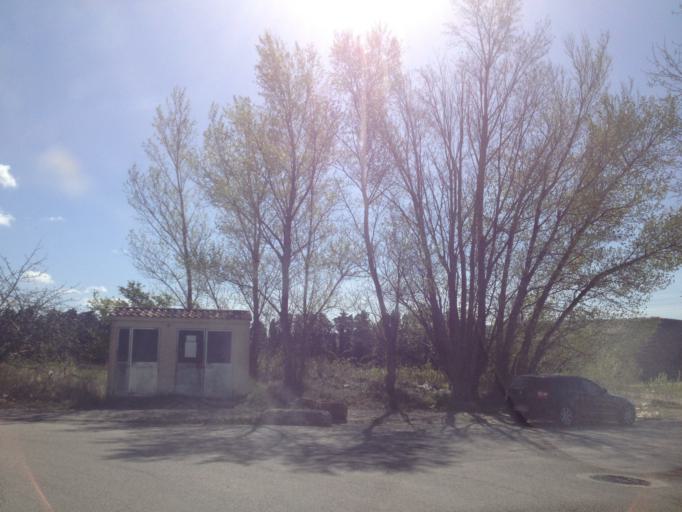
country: FR
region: Languedoc-Roussillon
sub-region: Departement du Gard
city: Les Angles
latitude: 43.9291
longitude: 4.7710
